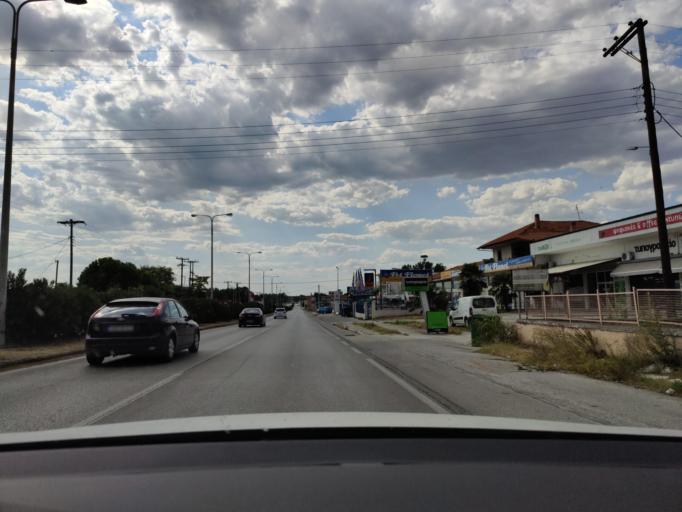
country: GR
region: Central Macedonia
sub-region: Nomos Serron
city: Lefkonas
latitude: 41.0896
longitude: 23.5207
